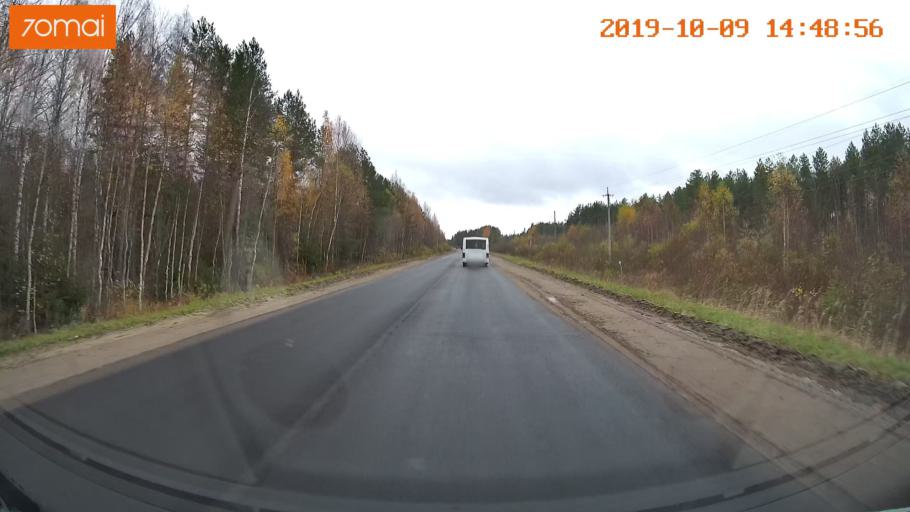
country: RU
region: Kostroma
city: Chistyye Bory
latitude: 58.3995
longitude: 41.5780
